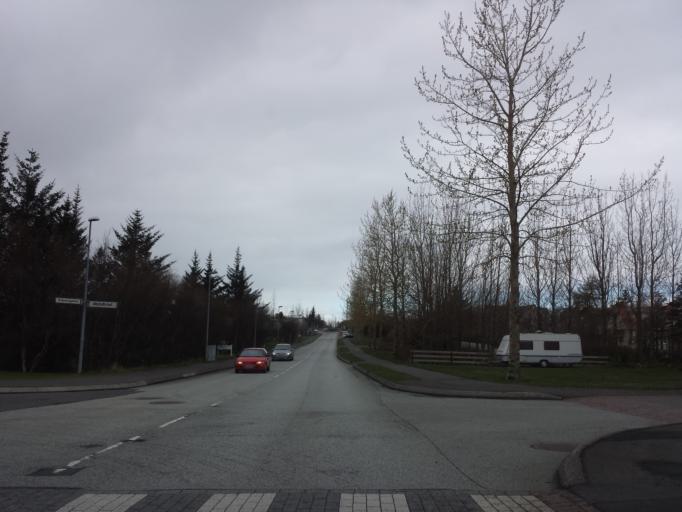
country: IS
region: Capital Region
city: Kopavogur
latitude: 64.1090
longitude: -21.9114
